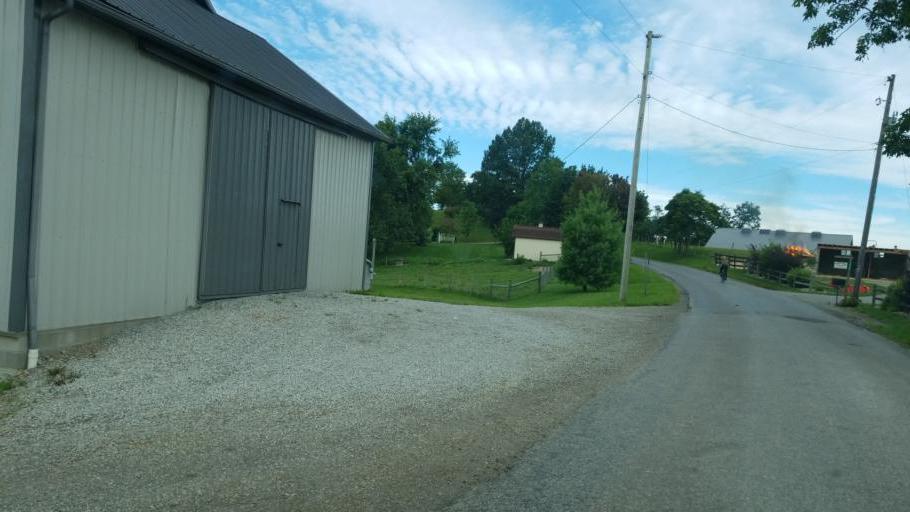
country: US
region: Ohio
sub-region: Holmes County
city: Millersburg
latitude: 40.5061
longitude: -81.8007
